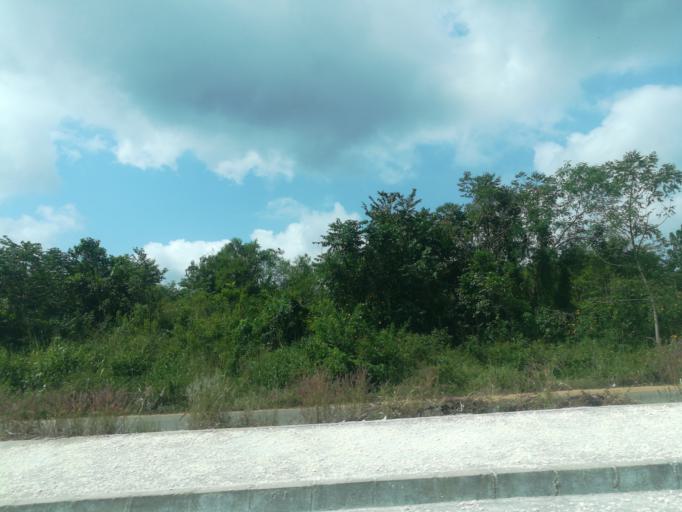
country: NG
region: Oyo
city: Moniya
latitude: 7.5855
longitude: 3.9128
